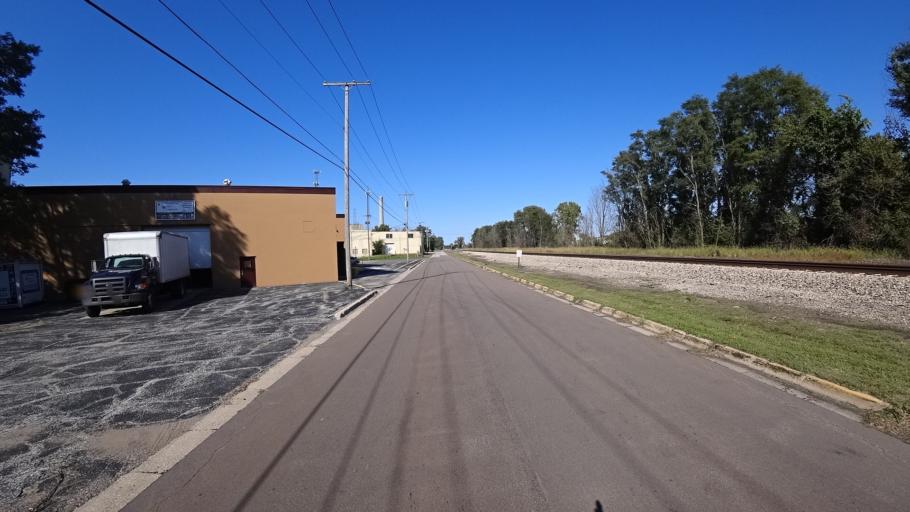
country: US
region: Indiana
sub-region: LaPorte County
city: Michigan City
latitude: 41.7132
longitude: -86.9089
